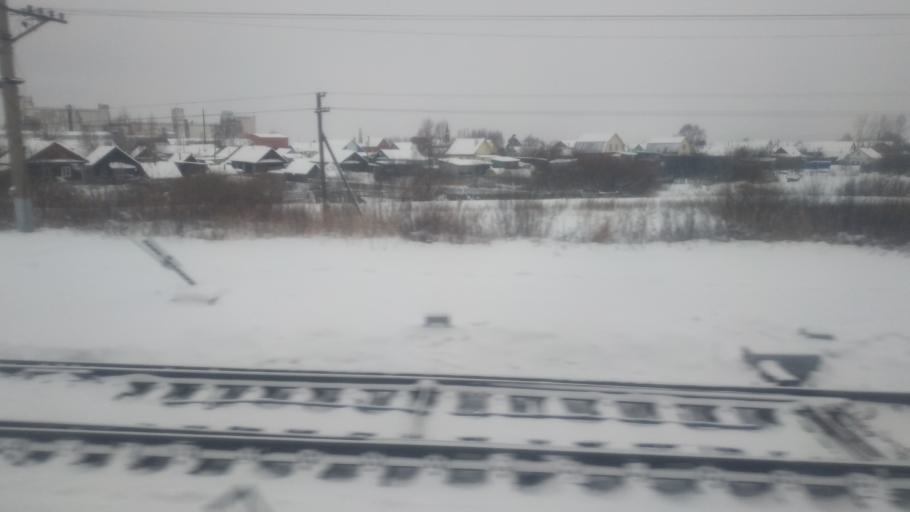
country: RU
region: Bashkortostan
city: Yanaul
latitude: 56.2756
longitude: 54.9407
